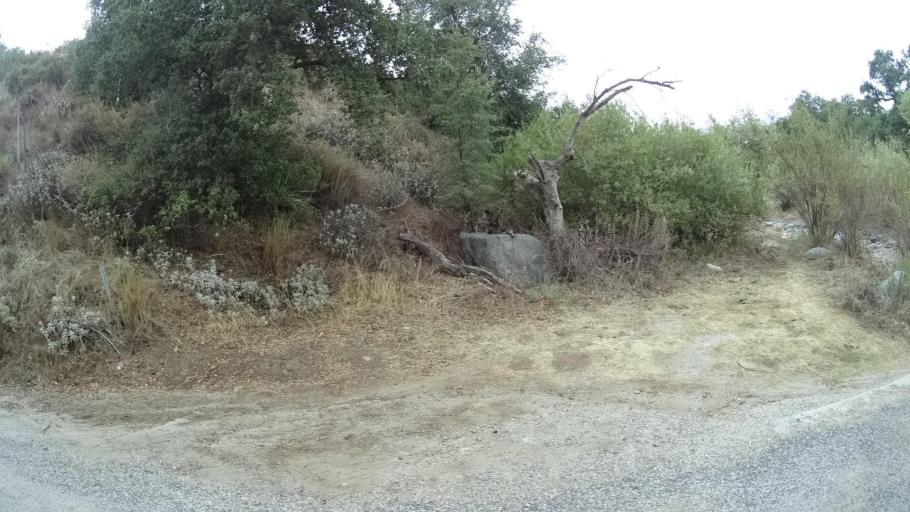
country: US
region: California
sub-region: San Diego County
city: Descanso
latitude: 32.9635
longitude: -116.6646
